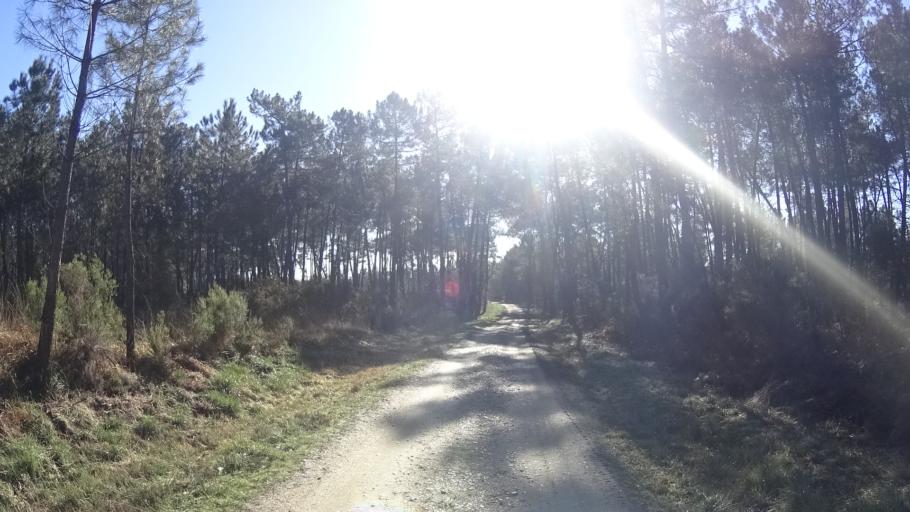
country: FR
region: Aquitaine
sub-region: Departement de la Dordogne
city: La Roche-Chalais
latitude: 45.1691
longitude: 0.0379
